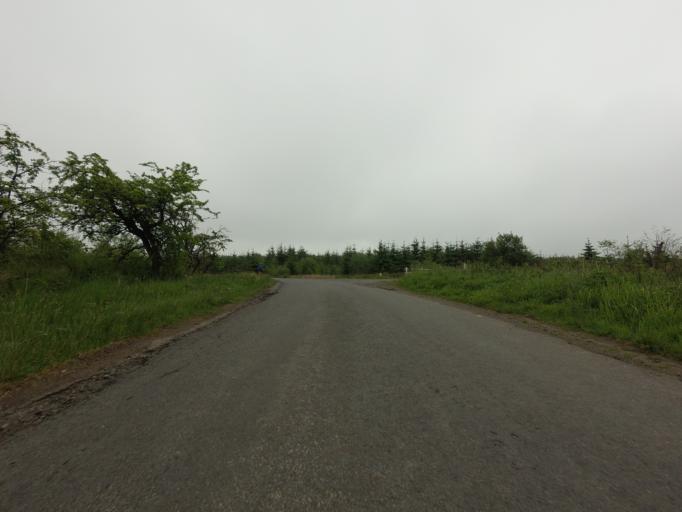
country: GB
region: Scotland
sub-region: Fife
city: Townhill
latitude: 56.1299
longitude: -3.4426
